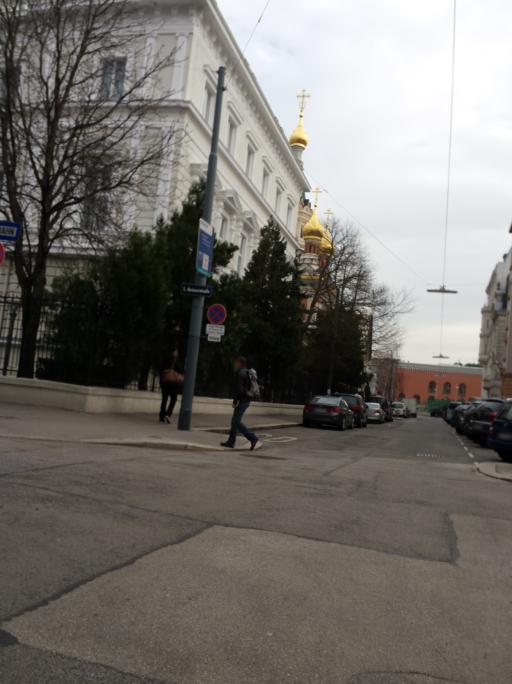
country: AT
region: Vienna
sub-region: Wien Stadt
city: Vienna
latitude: 48.1973
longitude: 16.3838
